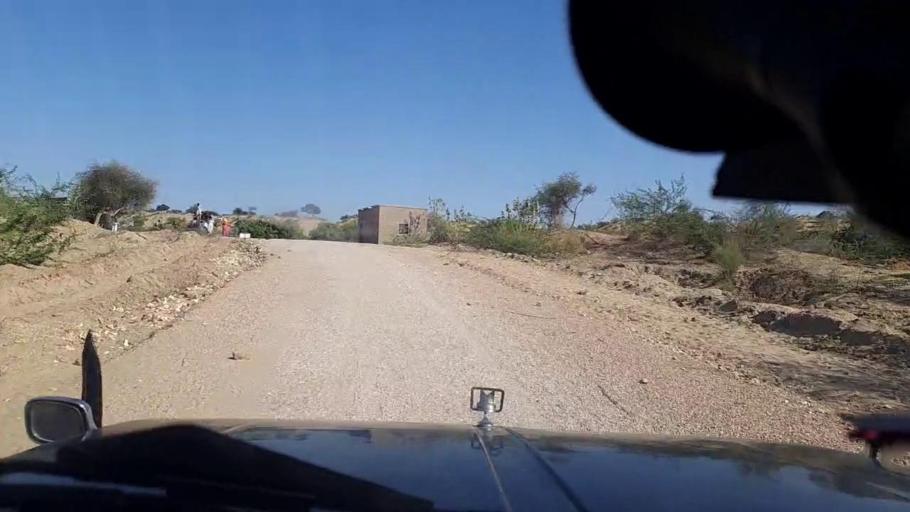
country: PK
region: Sindh
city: Diplo
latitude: 24.4683
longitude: 69.7952
